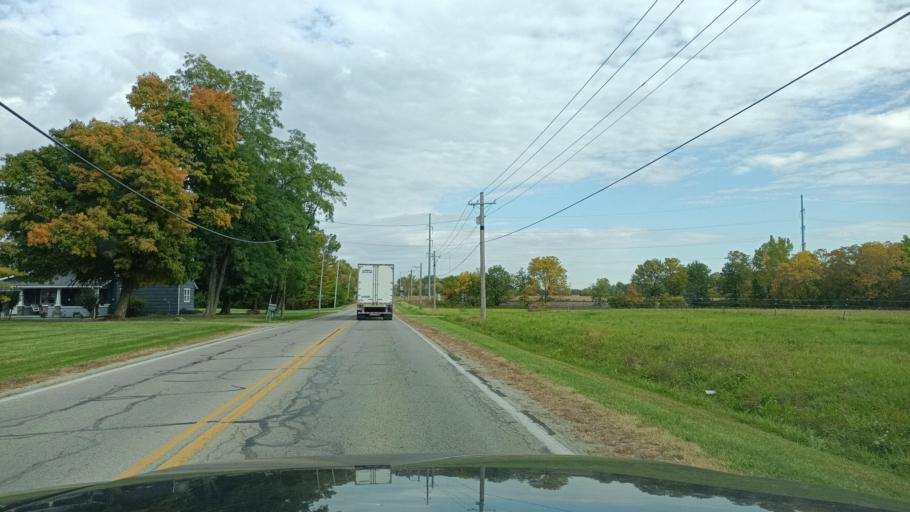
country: US
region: Indiana
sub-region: Delaware County
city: Yorktown
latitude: 40.2009
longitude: -85.4617
